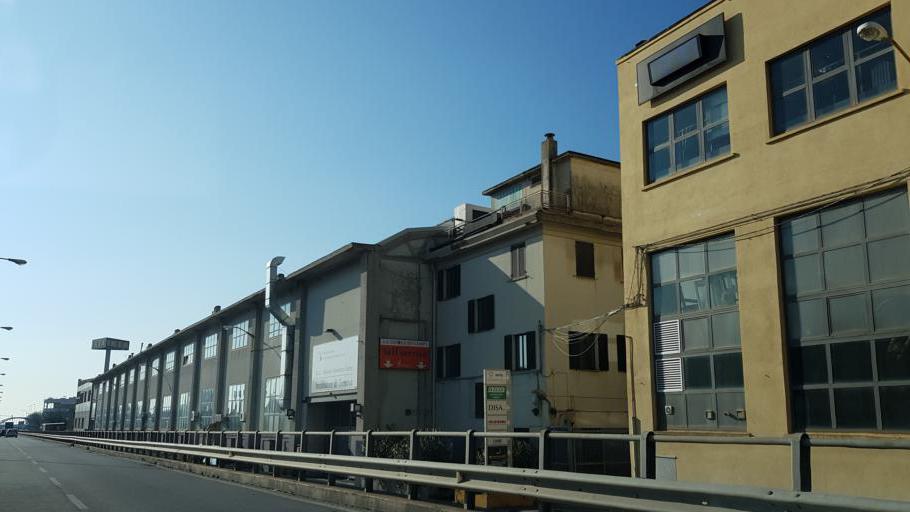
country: IT
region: Liguria
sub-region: Provincia di Genova
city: San Teodoro
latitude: 44.4256
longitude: 8.8871
